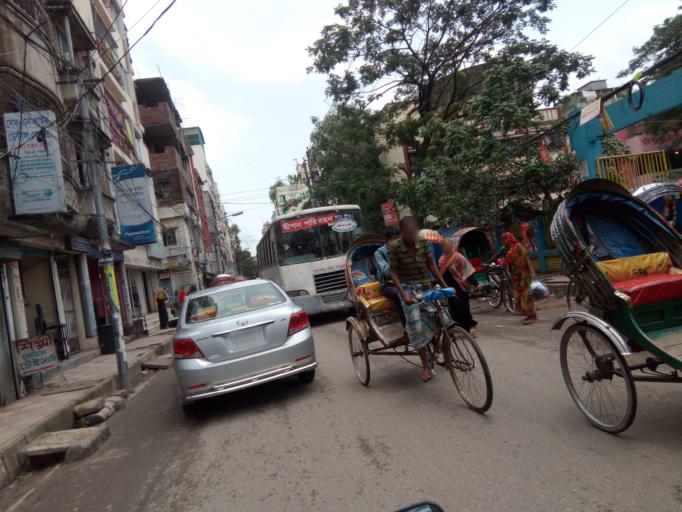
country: BD
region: Dhaka
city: Azimpur
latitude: 23.7611
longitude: 90.3633
